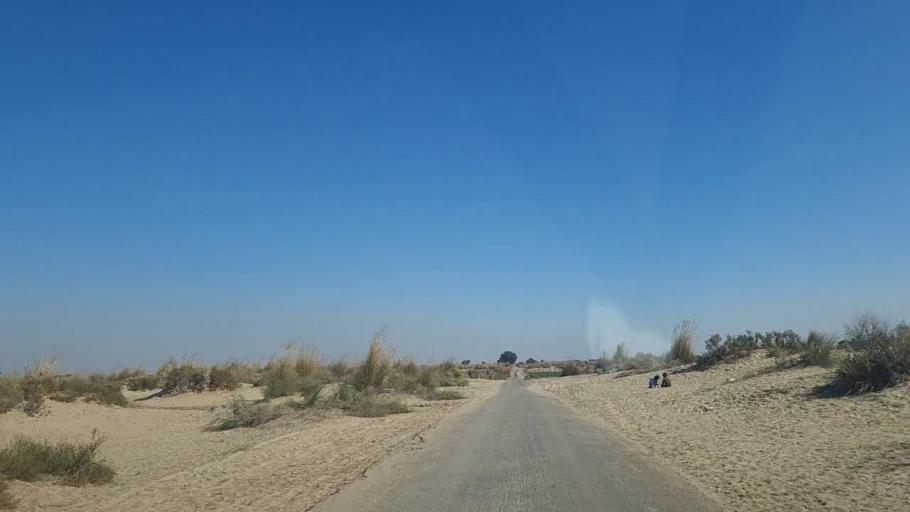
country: PK
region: Sindh
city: Khadro
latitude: 26.2093
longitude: 68.8521
